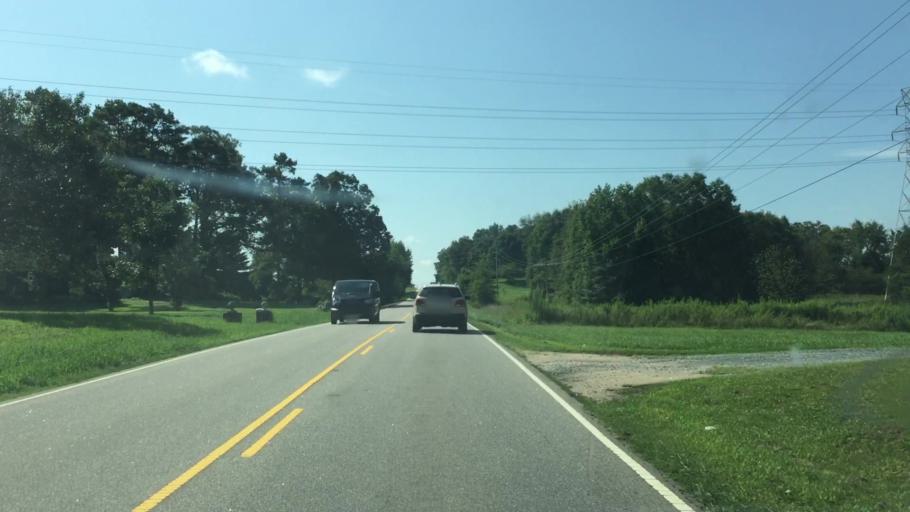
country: US
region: North Carolina
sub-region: Union County
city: Unionville
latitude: 35.1264
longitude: -80.4304
